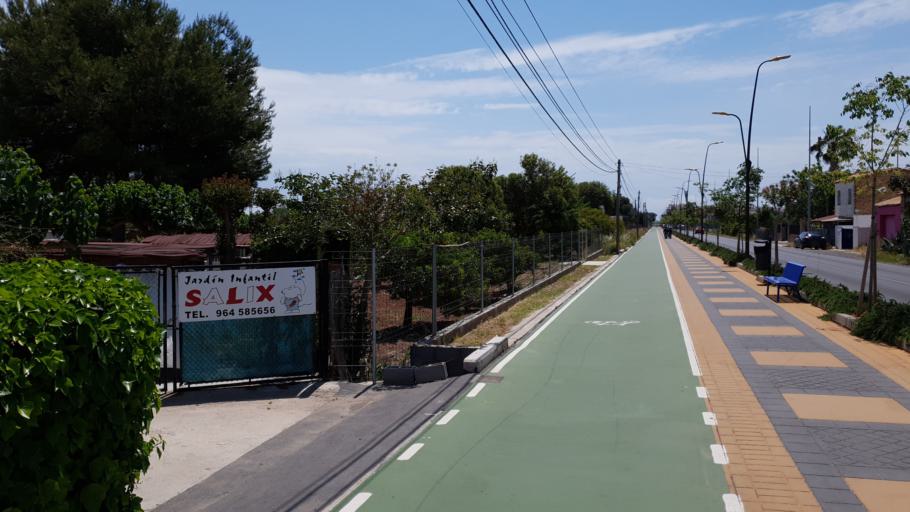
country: ES
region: Valencia
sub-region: Provincia de Castello
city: Burriana
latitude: 39.8761
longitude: -0.0770
